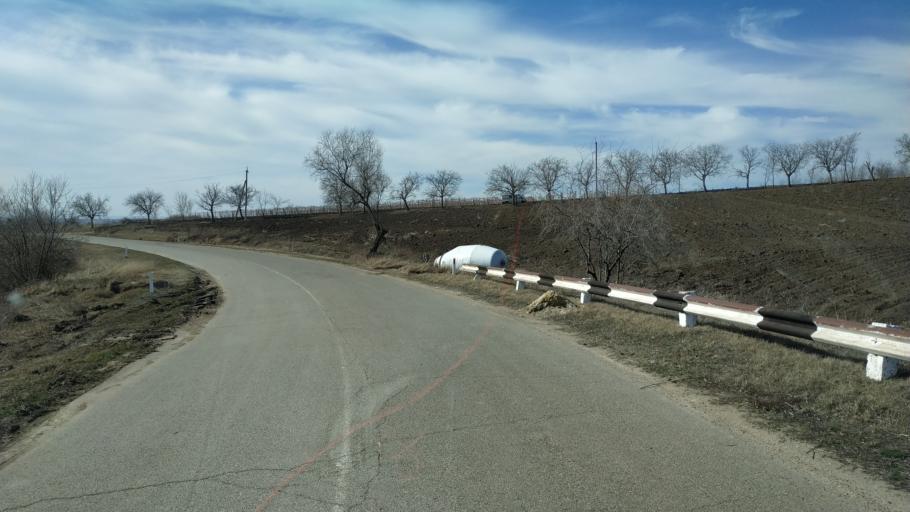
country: MD
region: Nisporeni
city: Nisporeni
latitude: 46.9560
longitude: 28.2285
